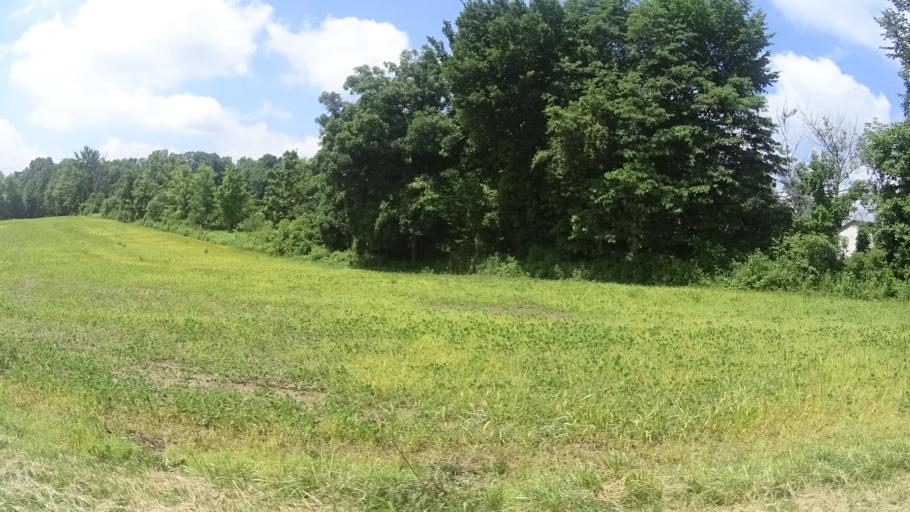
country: US
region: Ohio
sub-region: Huron County
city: Wakeman
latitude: 41.3036
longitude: -82.3579
